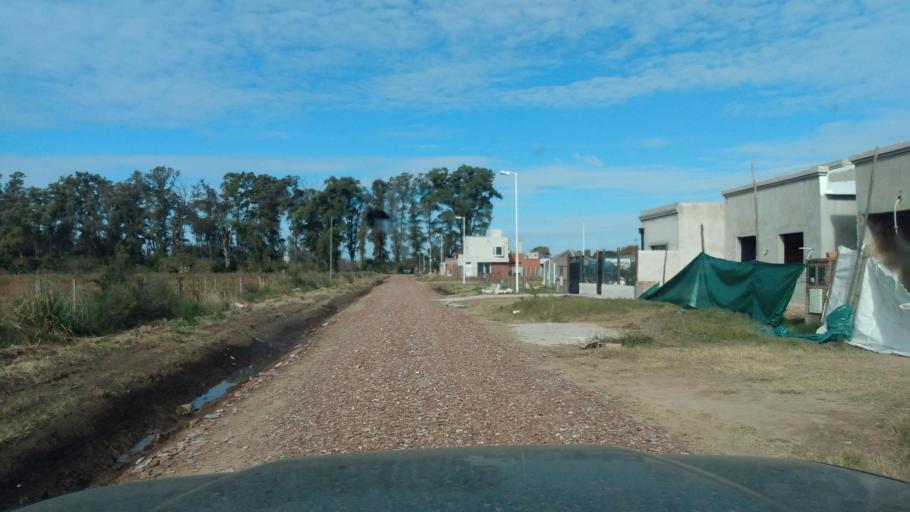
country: AR
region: Buenos Aires
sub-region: Partido de Lujan
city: Lujan
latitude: -34.5931
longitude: -59.1768
